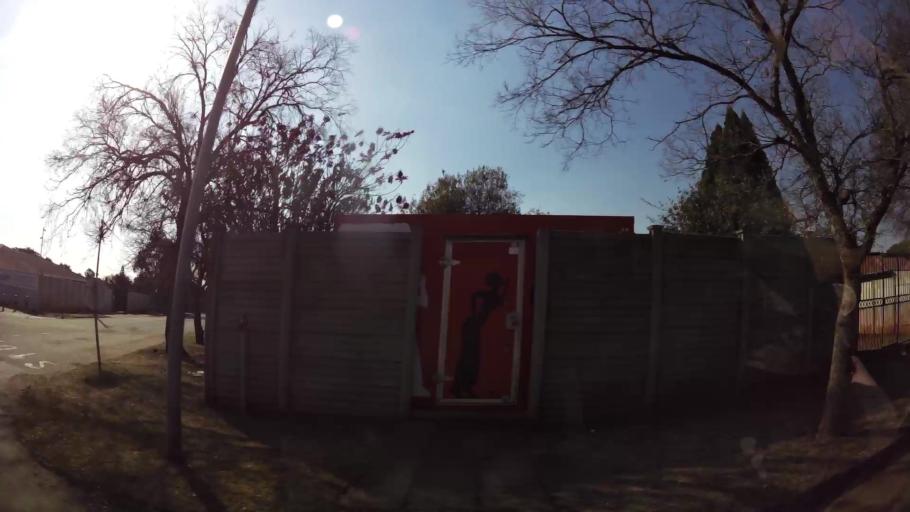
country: ZA
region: Gauteng
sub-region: West Rand District Municipality
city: Randfontein
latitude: -26.1847
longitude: 27.6930
